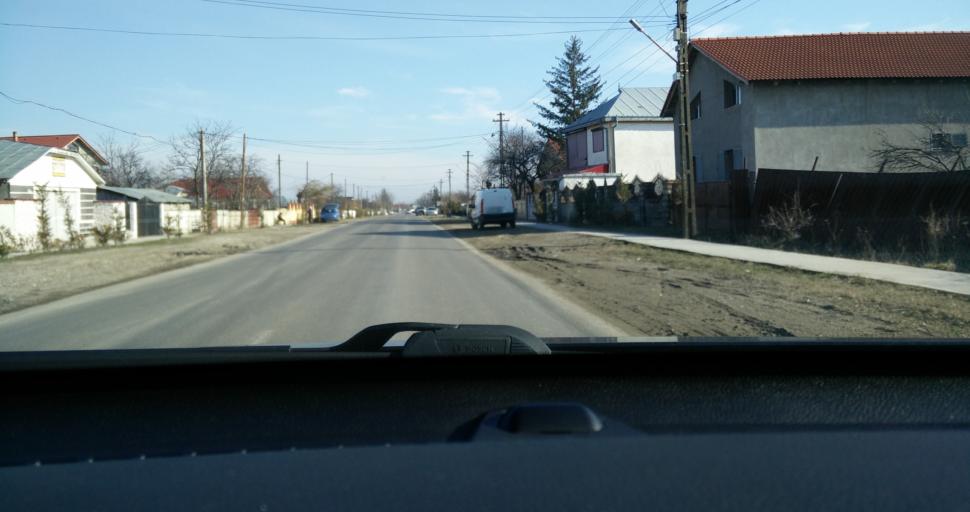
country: RO
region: Vrancea
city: Vulturu de Sus
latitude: 45.6219
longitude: 27.4054
